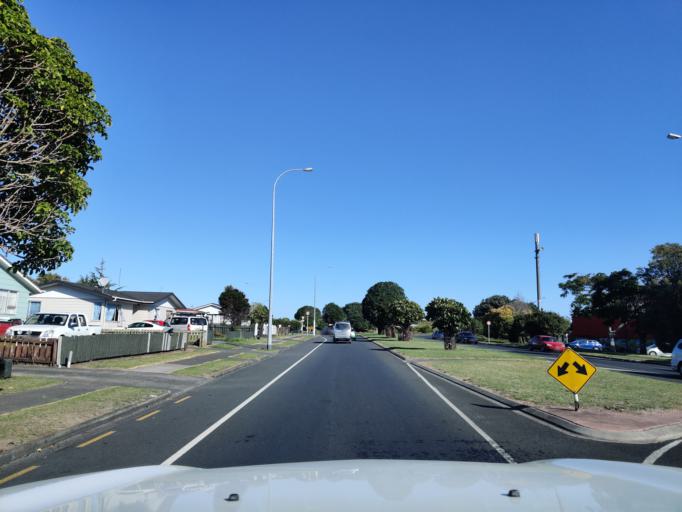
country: NZ
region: Auckland
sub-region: Auckland
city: Takanini
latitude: -37.0322
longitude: 174.8694
